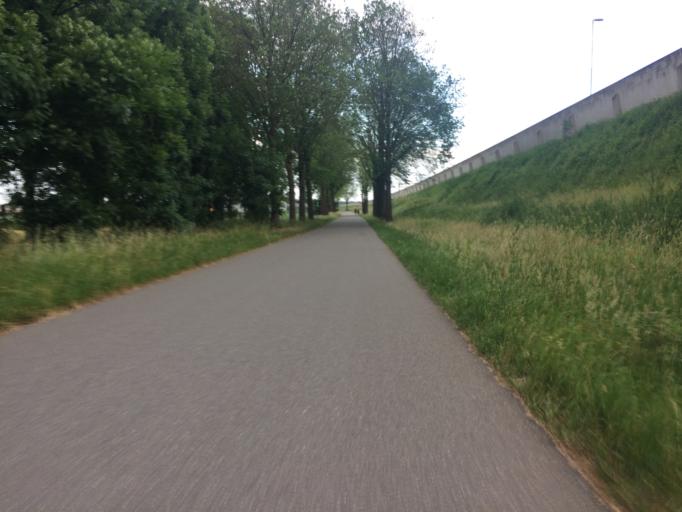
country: NL
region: North Brabant
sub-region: Gemeente 's-Hertogenbosch
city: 's-Hertogenbosch
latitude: 51.7347
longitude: 5.3097
